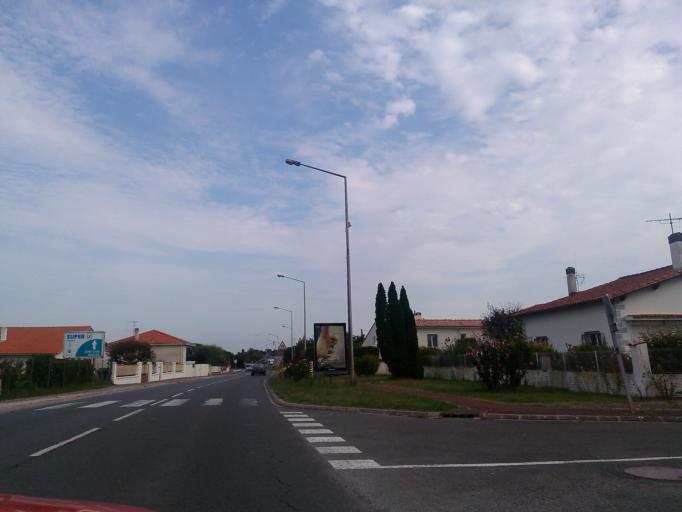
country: FR
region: Poitou-Charentes
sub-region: Departement de la Charente-Maritime
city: Saujon
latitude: 45.6748
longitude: -0.9447
